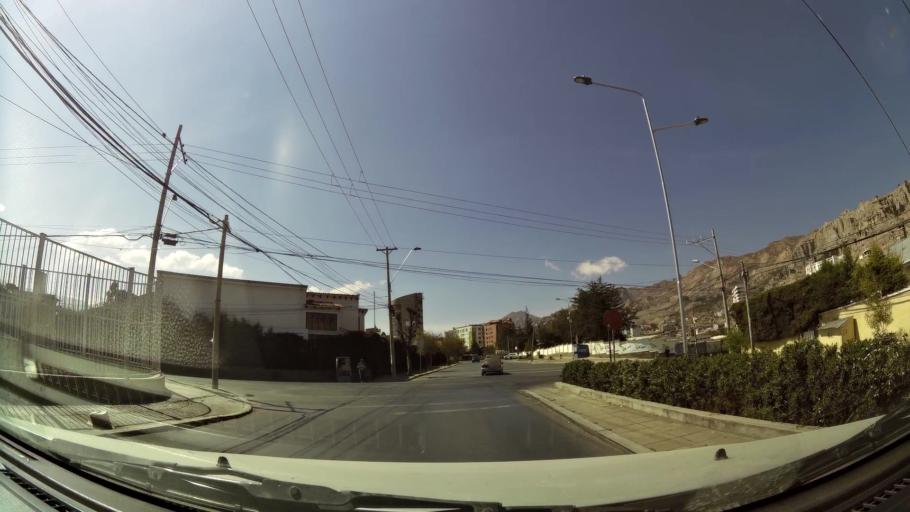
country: BO
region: La Paz
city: La Paz
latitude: -16.5441
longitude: -68.0832
